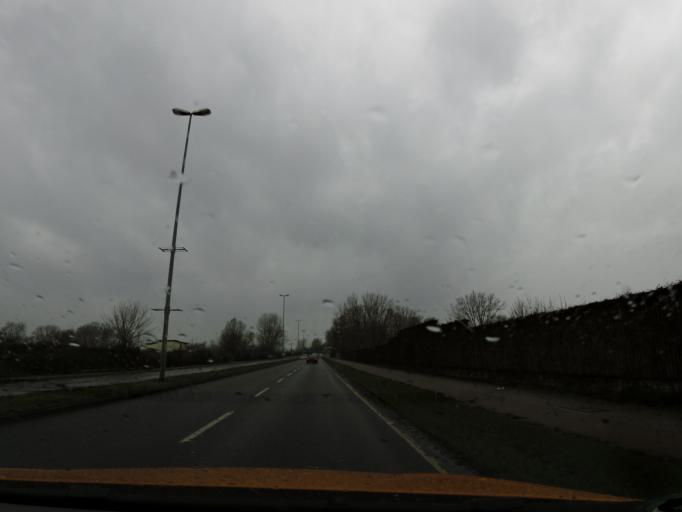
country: DE
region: Brandenburg
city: Brandenburg an der Havel
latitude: 52.4017
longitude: 12.5442
